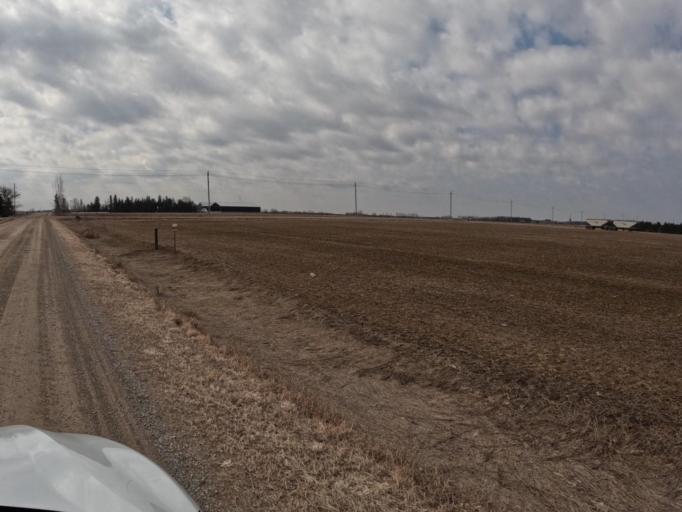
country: CA
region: Ontario
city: Orangeville
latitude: 43.9189
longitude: -80.2392
